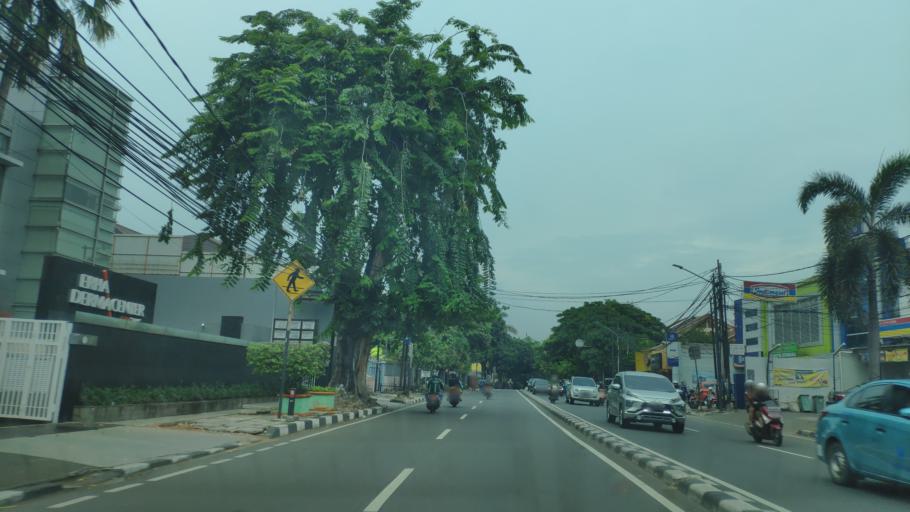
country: ID
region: Jakarta Raya
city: Jakarta
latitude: -6.1899
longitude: 106.7912
